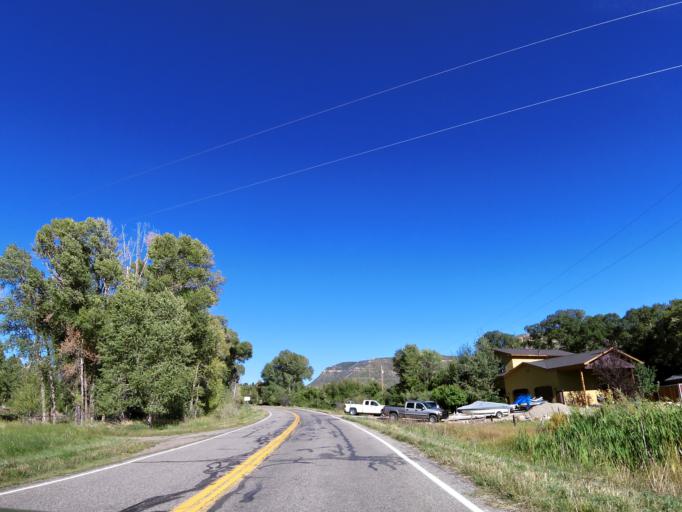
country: US
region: Colorado
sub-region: Montezuma County
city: Mancos
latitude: 37.3443
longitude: -108.2841
